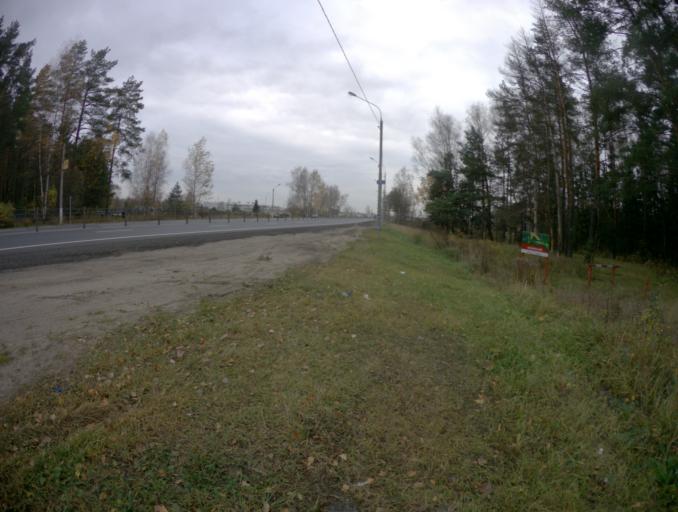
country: RU
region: Moskovskaya
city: Malaya Dubna
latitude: 55.8689
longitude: 38.9642
